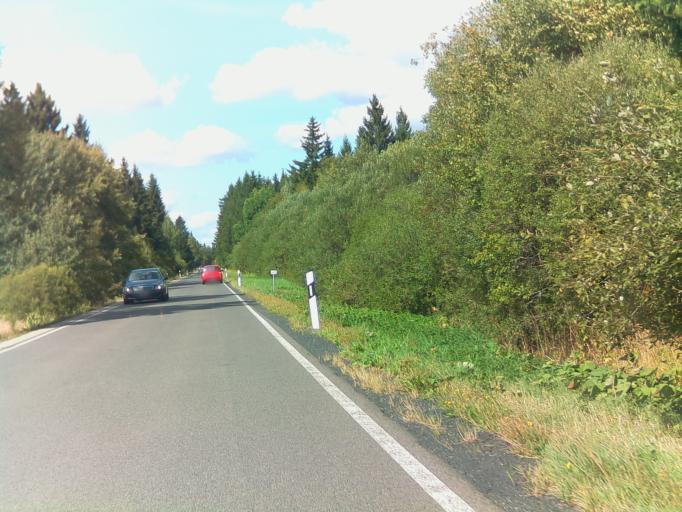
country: DE
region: Thuringia
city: Frankenheim
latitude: 50.5168
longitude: 10.0731
